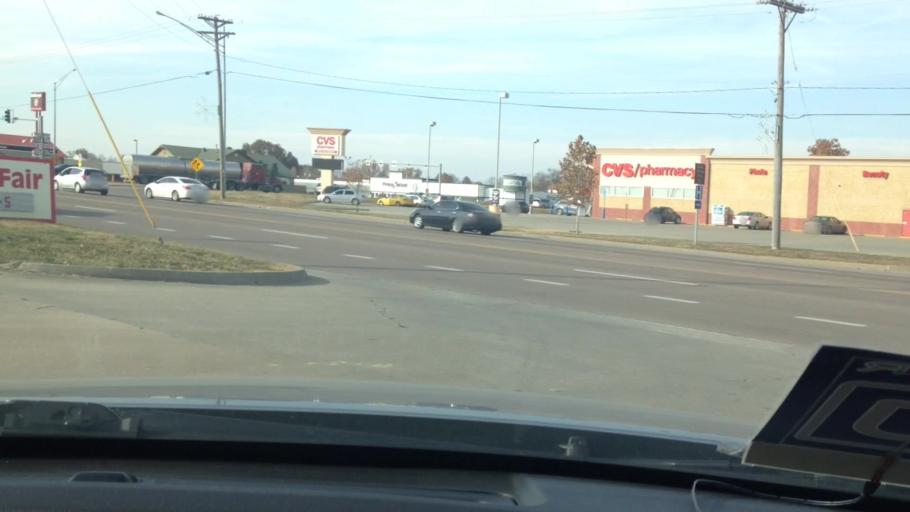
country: US
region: Missouri
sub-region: Henry County
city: Clinton
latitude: 38.3659
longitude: -93.7509
